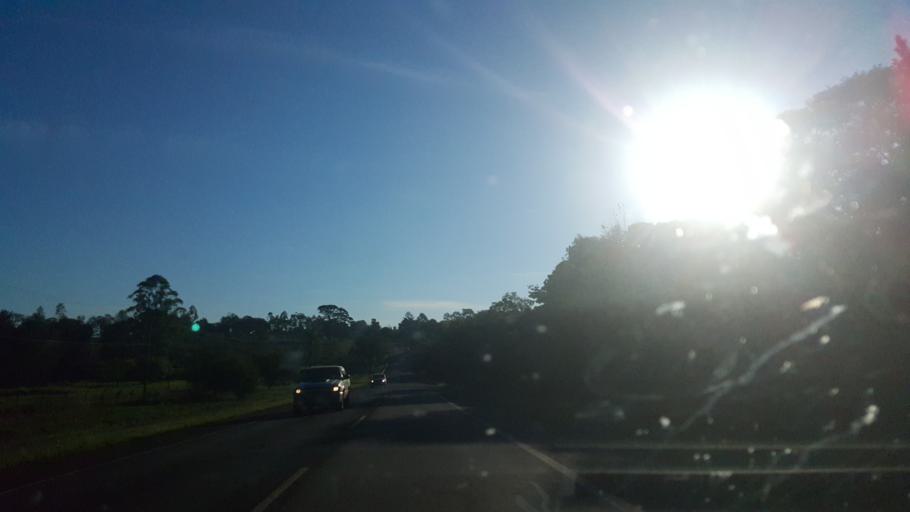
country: AR
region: Misiones
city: El Alcazar
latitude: -26.6711
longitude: -54.7757
